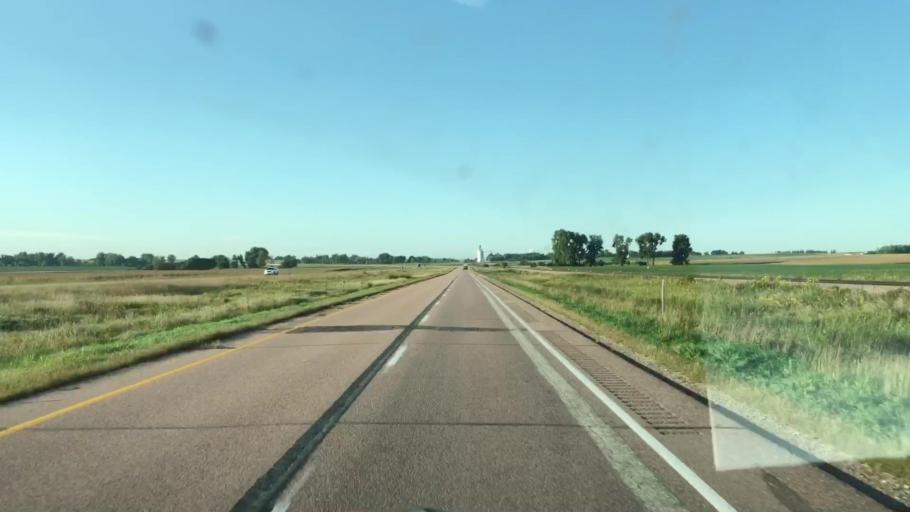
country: US
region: Iowa
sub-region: Osceola County
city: Sibley
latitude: 43.3382
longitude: -95.7770
